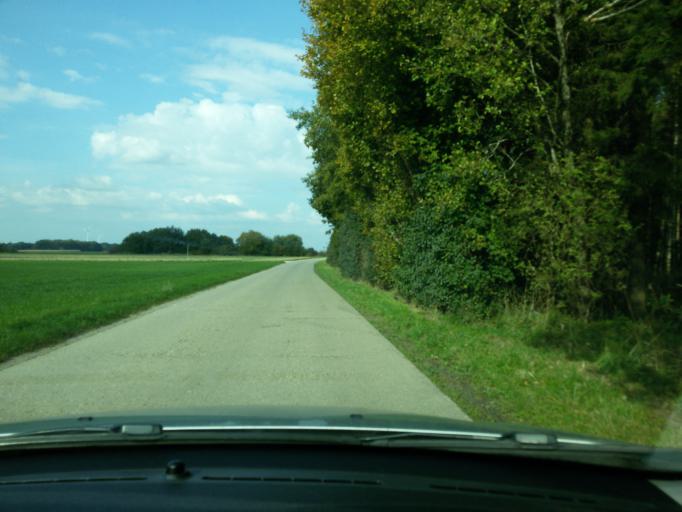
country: DE
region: Bavaria
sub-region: Swabia
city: Lamerdingen
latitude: 48.0664
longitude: 10.7796
